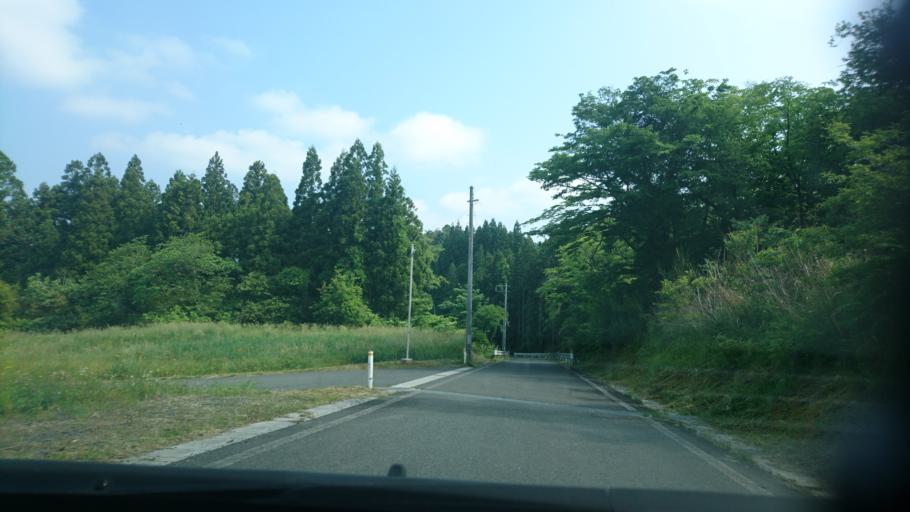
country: JP
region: Iwate
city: Ichinoseki
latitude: 38.9050
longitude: 141.2314
